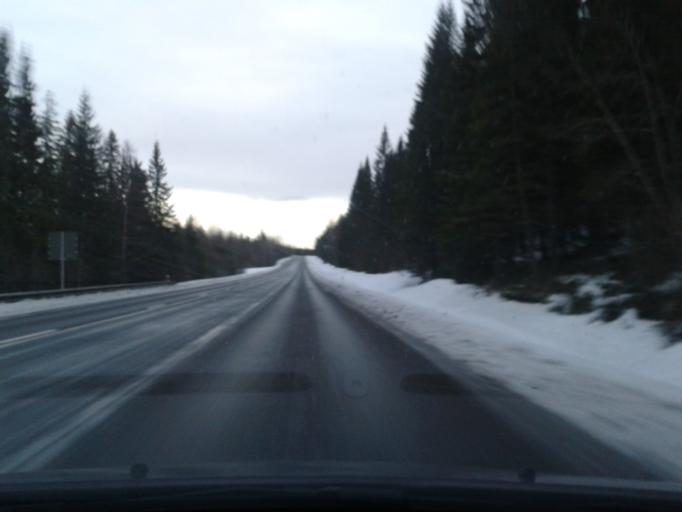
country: SE
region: Vaesternorrland
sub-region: Solleftea Kommun
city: Solleftea
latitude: 63.1354
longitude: 17.4540
